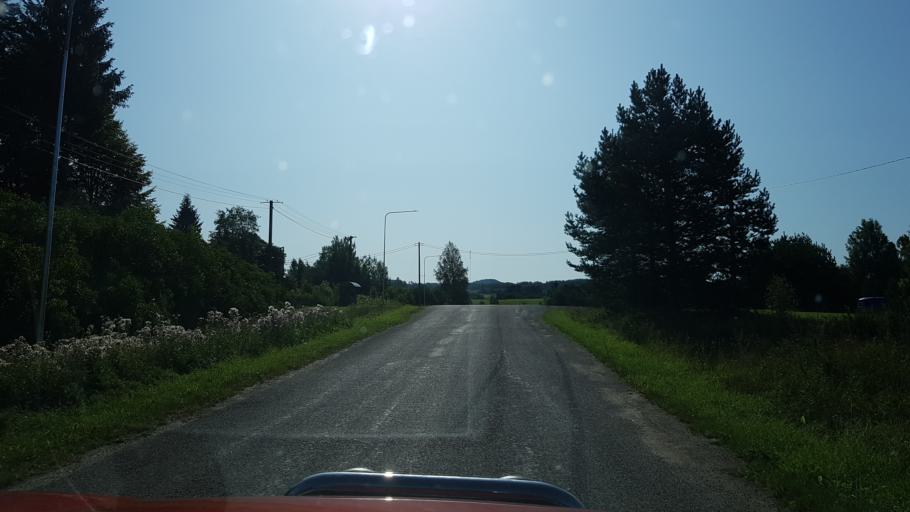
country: LV
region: Apes Novads
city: Ape
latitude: 57.6100
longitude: 26.8325
